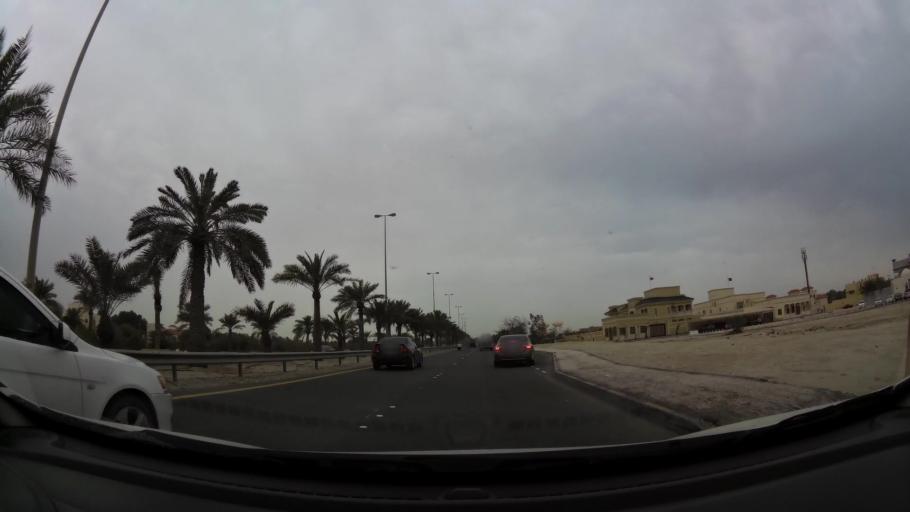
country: BH
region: Northern
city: Ar Rifa'
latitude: 26.1395
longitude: 50.5390
